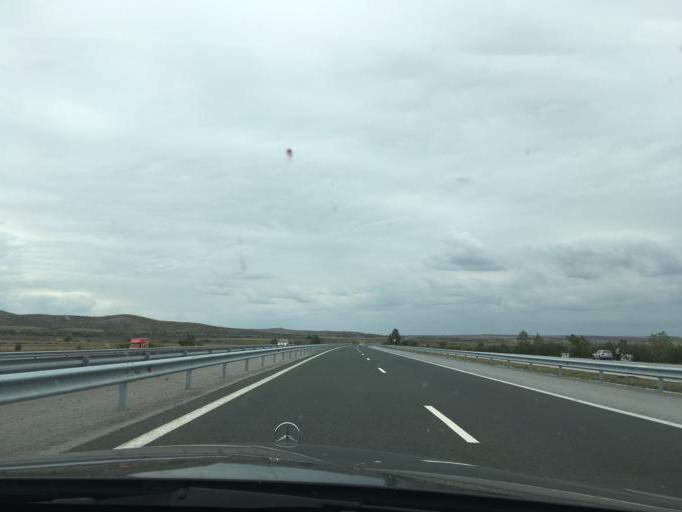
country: BG
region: Sliven
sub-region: Obshtina Sliven
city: Kermen
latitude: 42.5035
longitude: 26.3061
